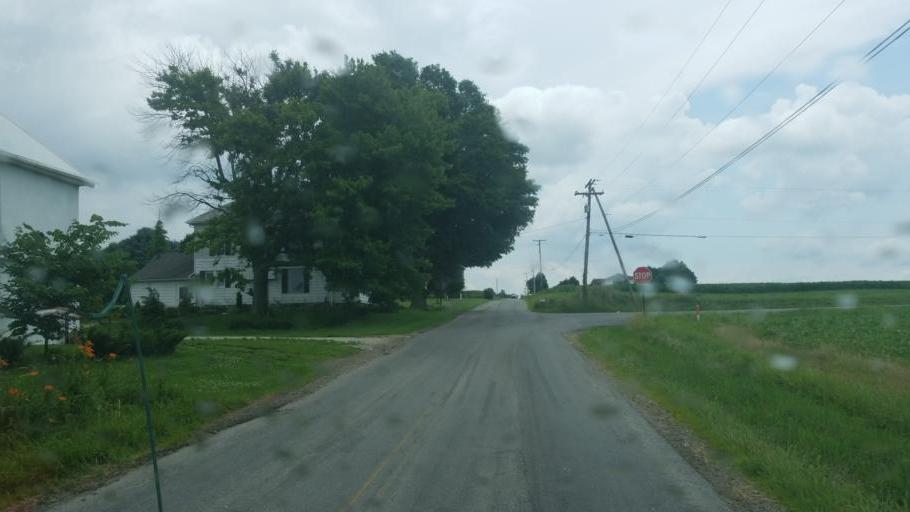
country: US
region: Ohio
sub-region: Wayne County
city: West Salem
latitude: 40.8579
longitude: -82.1038
